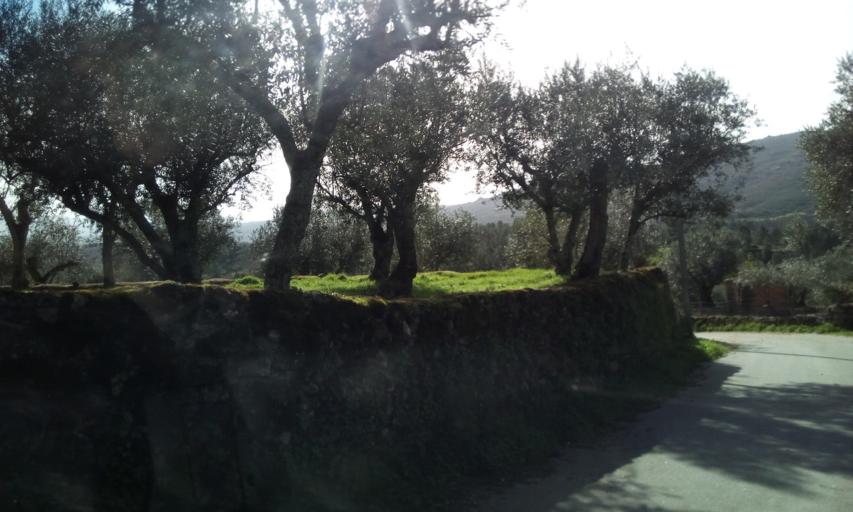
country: PT
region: Guarda
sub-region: Celorico da Beira
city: Celorico da Beira
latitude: 40.6552
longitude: -7.4110
